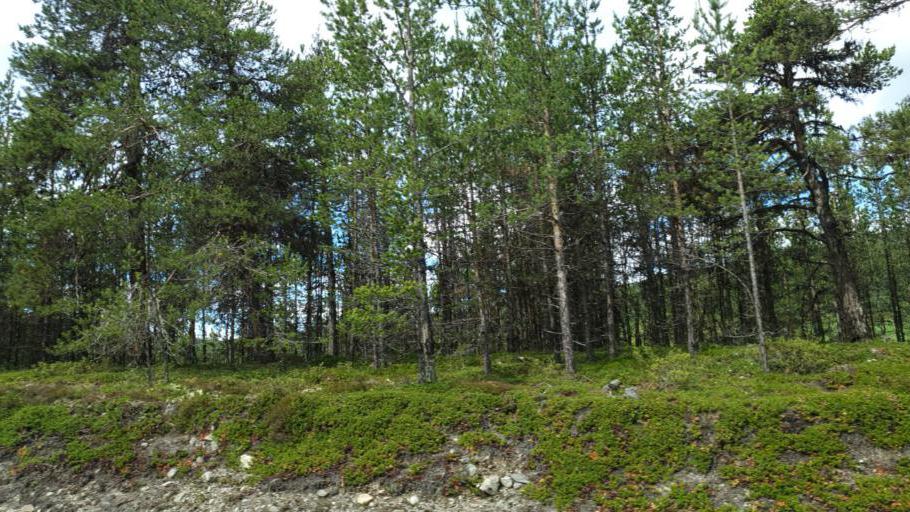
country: NO
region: Oppland
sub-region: Vaga
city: Vagamo
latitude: 61.7206
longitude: 9.0581
